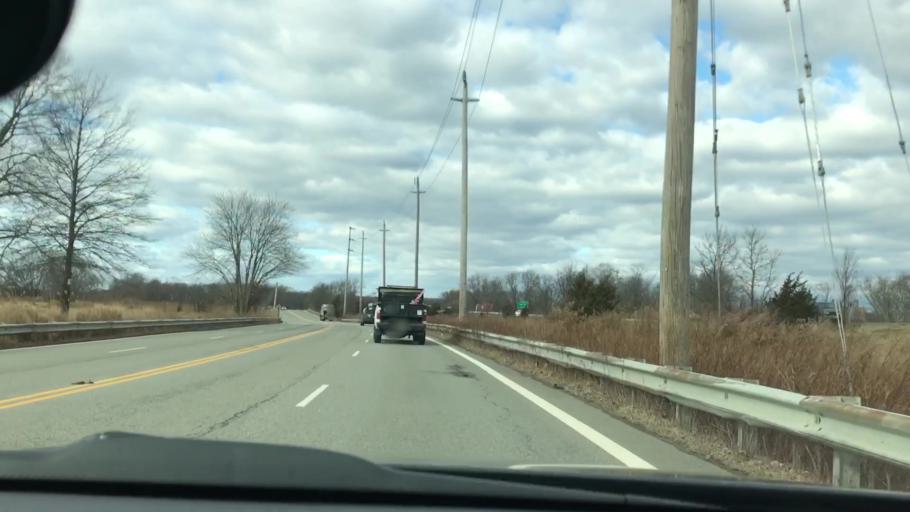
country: US
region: New Jersey
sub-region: Morris County
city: East Hanover
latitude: 40.8429
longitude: -74.3447
